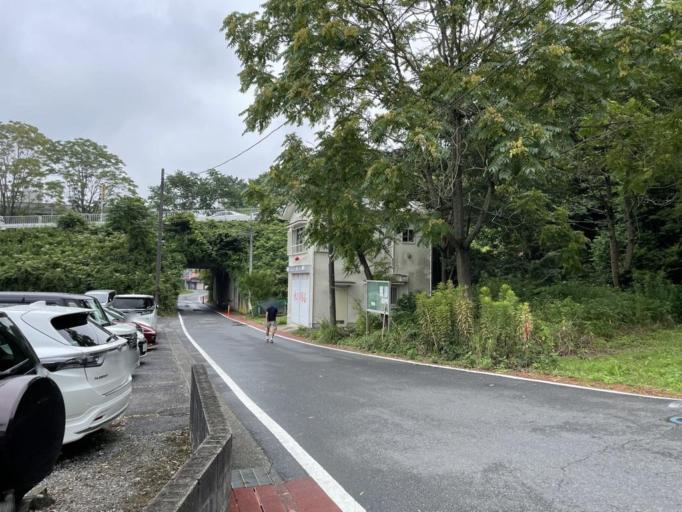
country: JP
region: Chiba
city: Sakura
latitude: 35.7244
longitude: 140.2244
